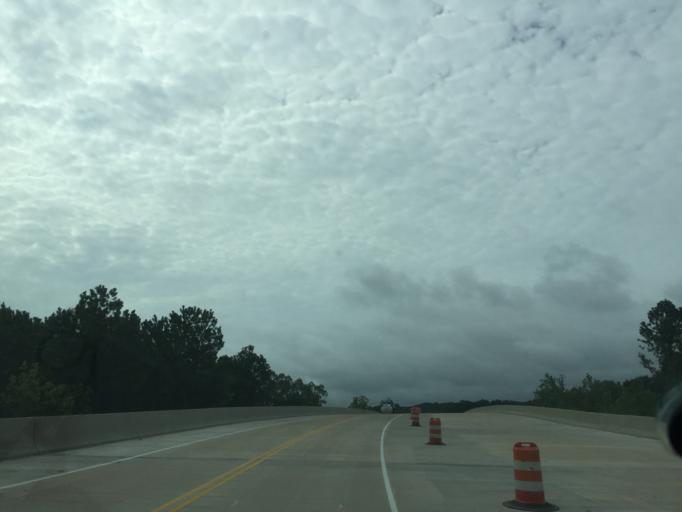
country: US
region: Mississippi
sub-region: Rankin County
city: Brandon
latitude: 32.2895
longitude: -89.9939
